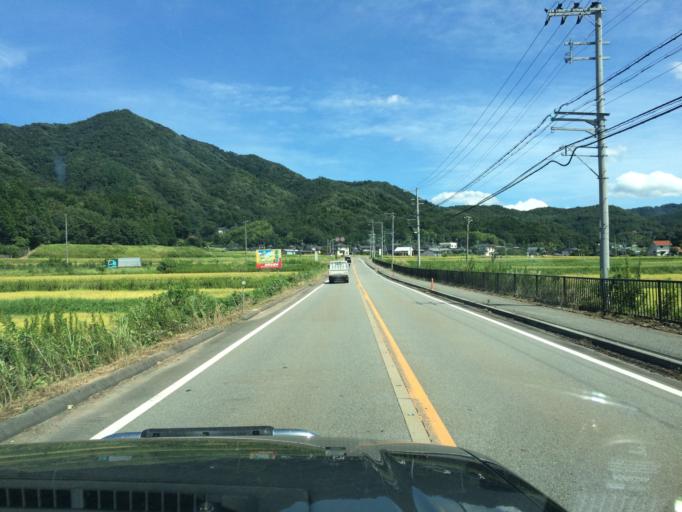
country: JP
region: Hyogo
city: Toyooka
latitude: 35.4372
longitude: 134.7981
